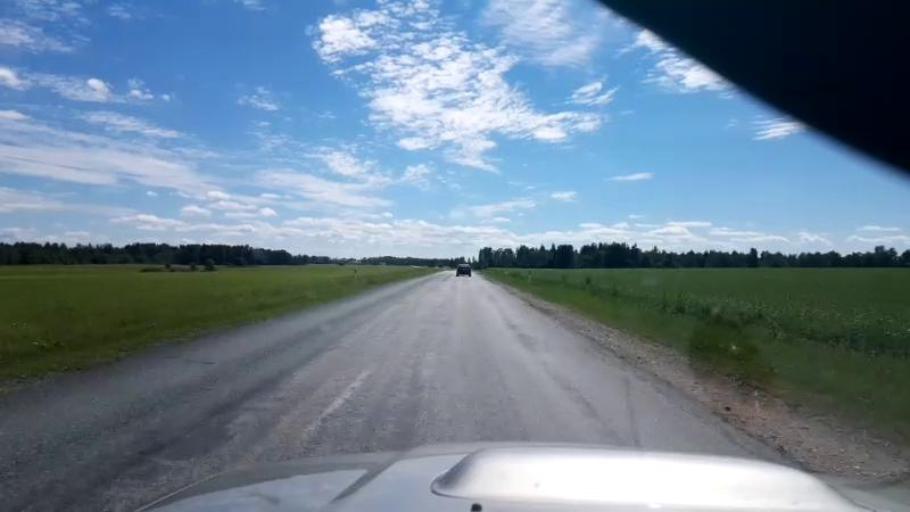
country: EE
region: Jogevamaa
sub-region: Jogeva linn
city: Jogeva
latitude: 58.8318
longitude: 26.2878
